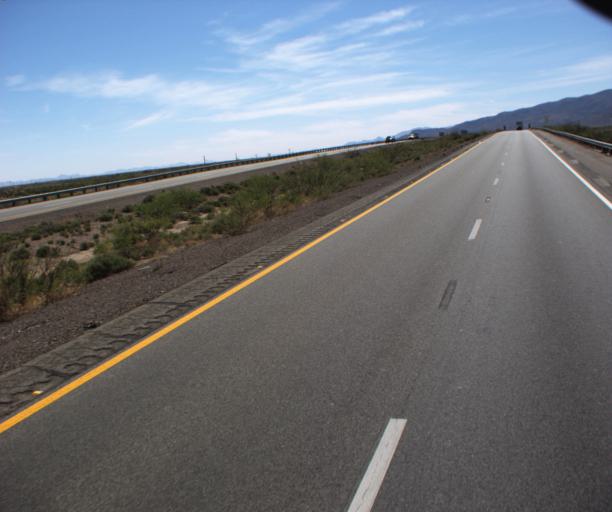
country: US
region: Arizona
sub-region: Cochise County
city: Willcox
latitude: 32.3552
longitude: -109.6110
